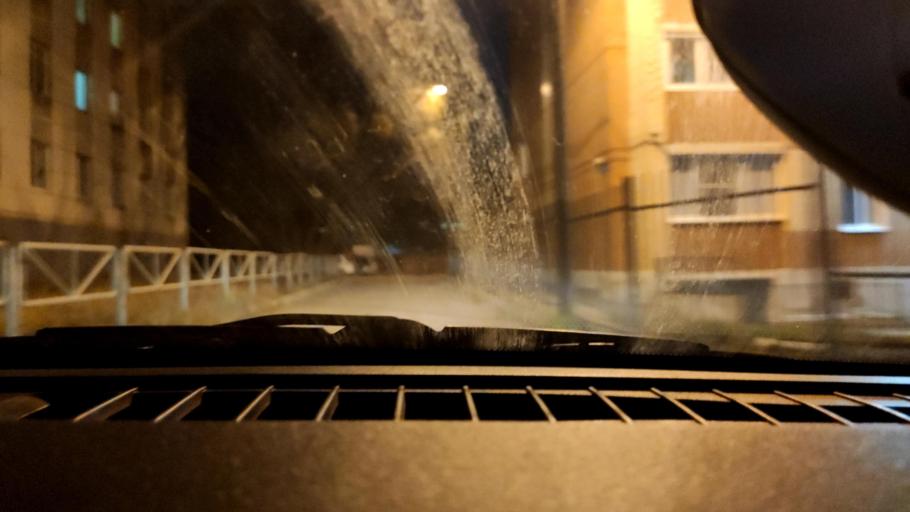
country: RU
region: Perm
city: Perm
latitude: 57.9600
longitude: 56.2206
